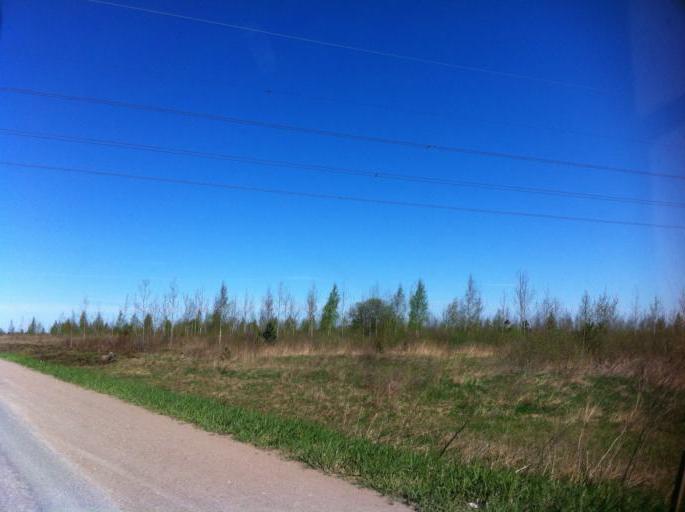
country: RU
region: Pskov
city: Pskov
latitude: 57.7998
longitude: 28.1951
